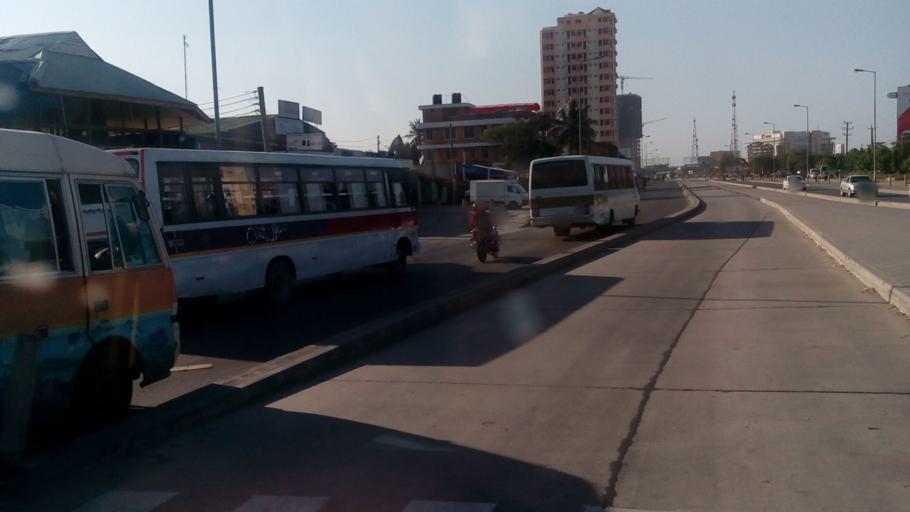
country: TZ
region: Dar es Salaam
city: Magomeni
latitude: -6.7850
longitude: 39.2635
